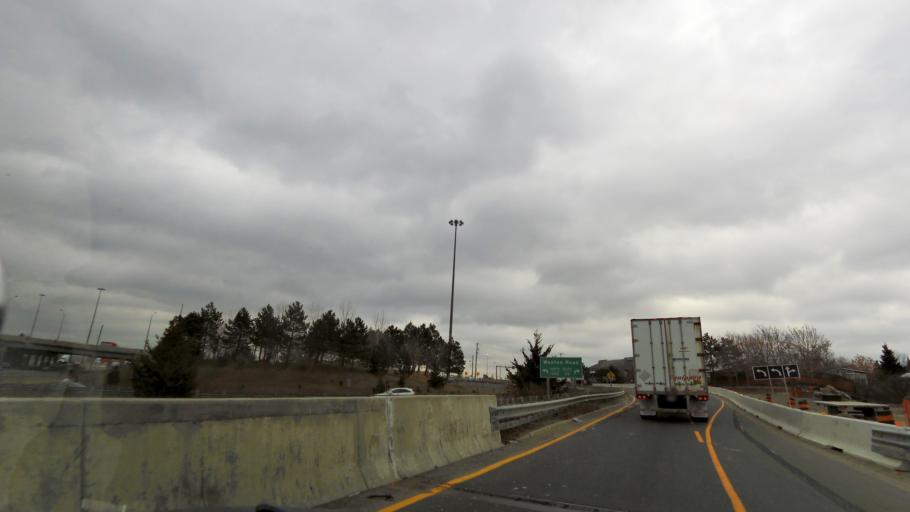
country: CA
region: Ontario
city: Etobicoke
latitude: 43.7120
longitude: -79.5378
